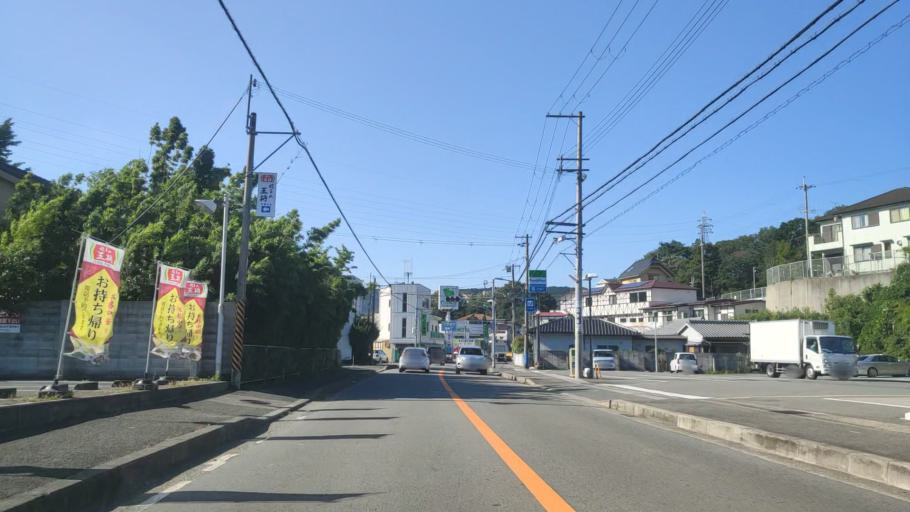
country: JP
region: Hyogo
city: Kobe
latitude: 34.7274
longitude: 135.1600
